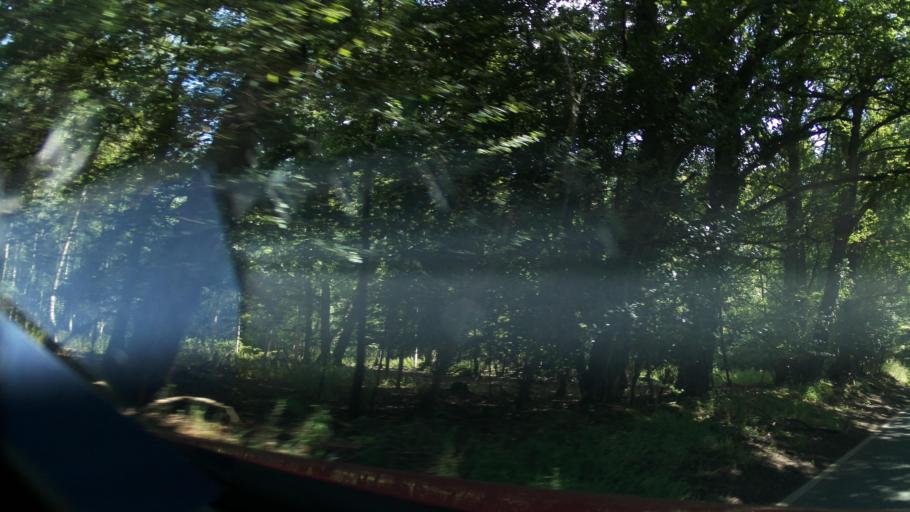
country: GB
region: England
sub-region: West Berkshire
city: Winterbourne
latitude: 51.4327
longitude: -1.3333
